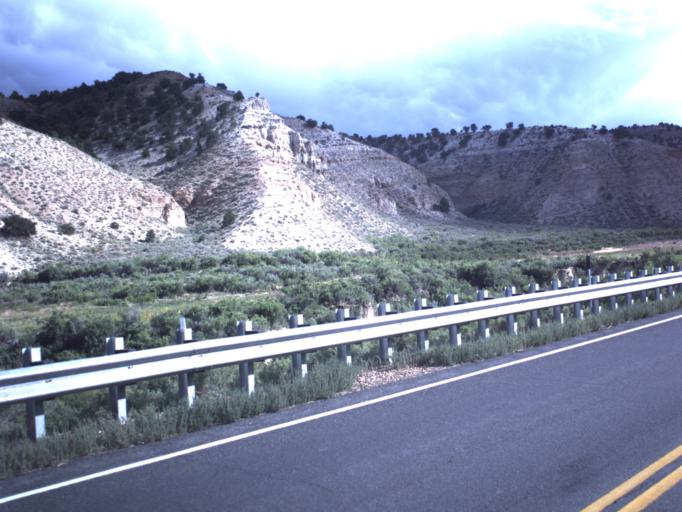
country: US
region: Utah
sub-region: Duchesne County
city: Duchesne
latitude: 40.1182
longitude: -110.4500
